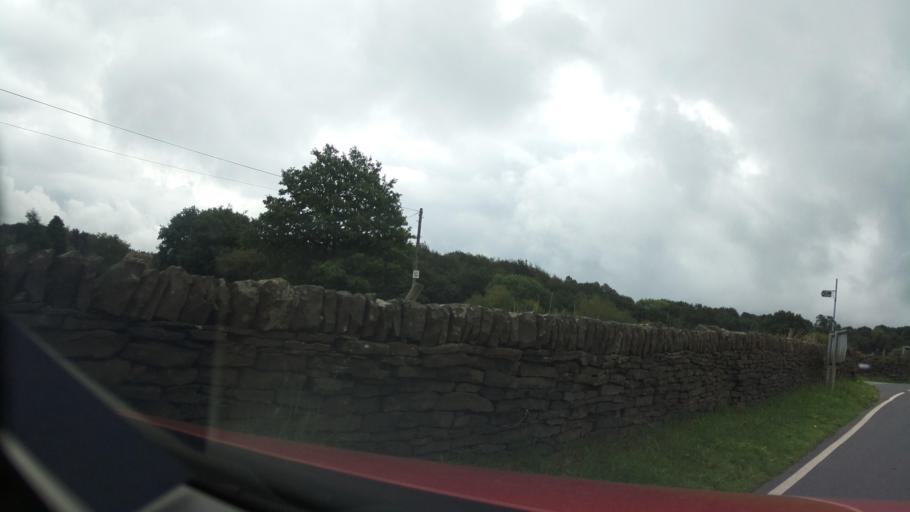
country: GB
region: England
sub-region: Kirklees
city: Shelley
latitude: 53.5841
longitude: -1.6874
